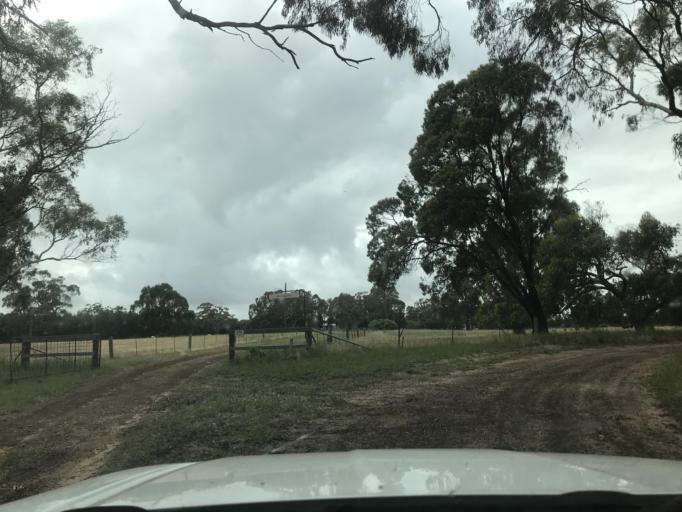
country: AU
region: South Australia
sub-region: Wattle Range
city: Penola
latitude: -37.1159
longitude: 141.0762
